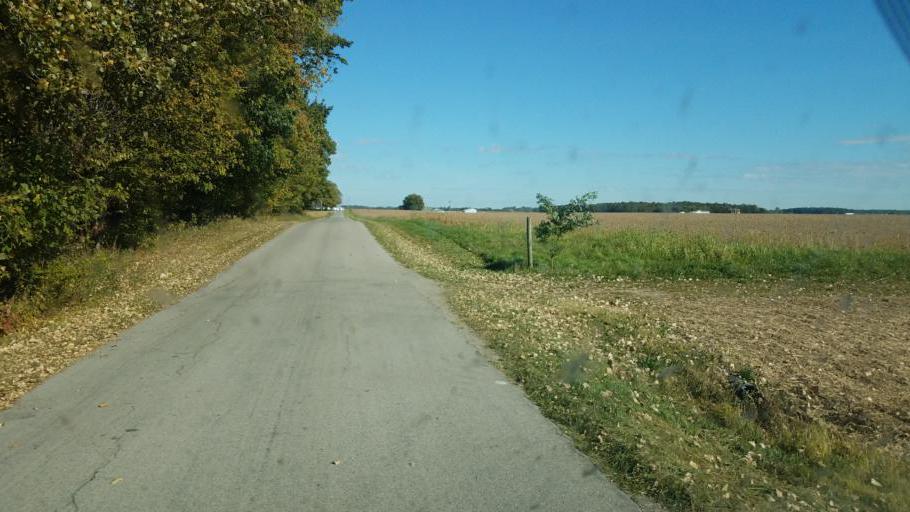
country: US
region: Ohio
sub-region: Wyandot County
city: Upper Sandusky
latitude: 40.7963
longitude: -83.2173
